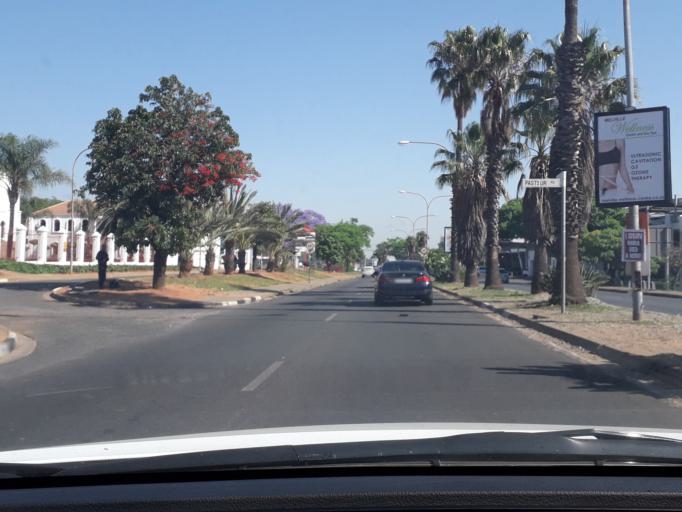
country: ZA
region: Gauteng
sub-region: City of Johannesburg Metropolitan Municipality
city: Johannesburg
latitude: -26.1320
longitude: 27.9729
